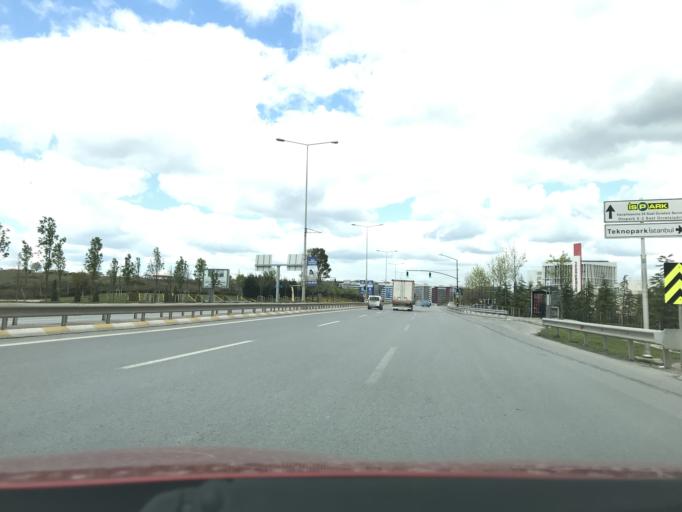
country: TR
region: Istanbul
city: Pendik
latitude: 40.9183
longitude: 29.3119
